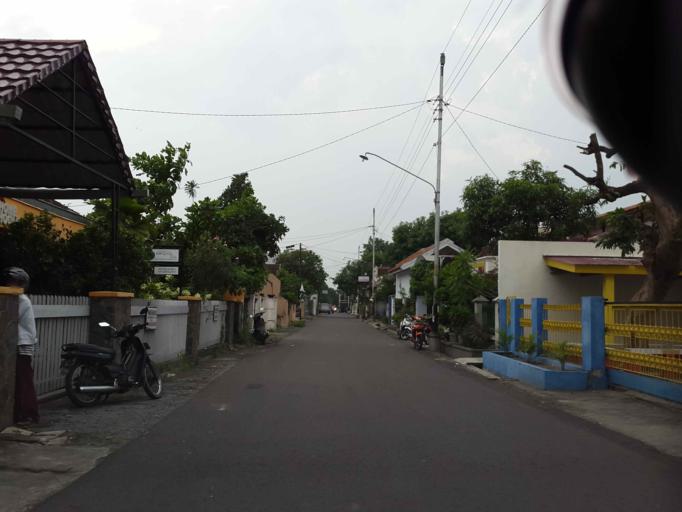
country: ID
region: Central Java
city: Surakarta
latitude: -7.5542
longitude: 110.8126
